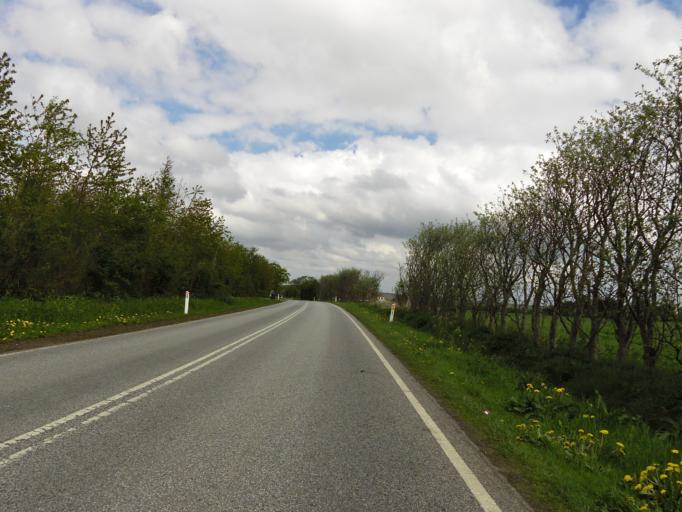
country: DK
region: South Denmark
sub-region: Haderslev Kommune
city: Gram
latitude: 55.2370
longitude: 8.9646
